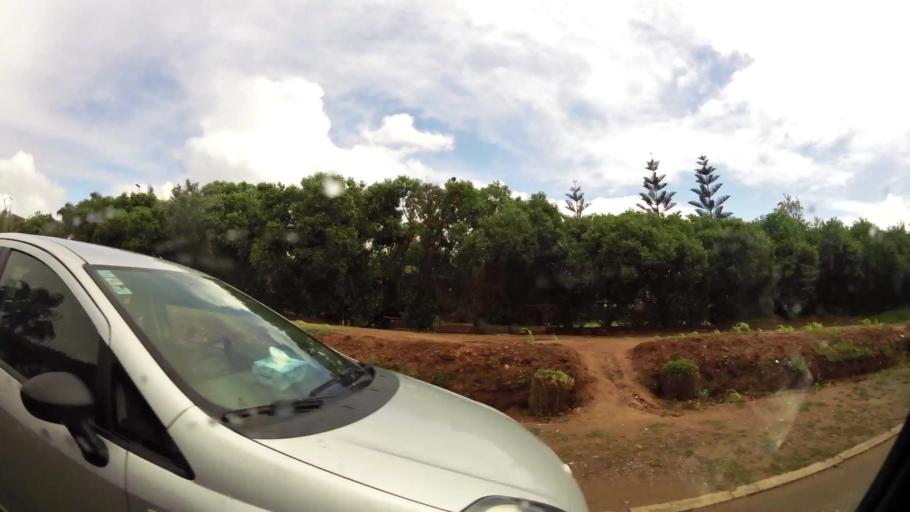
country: MA
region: Grand Casablanca
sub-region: Casablanca
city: Casablanca
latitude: 33.5342
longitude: -7.6407
